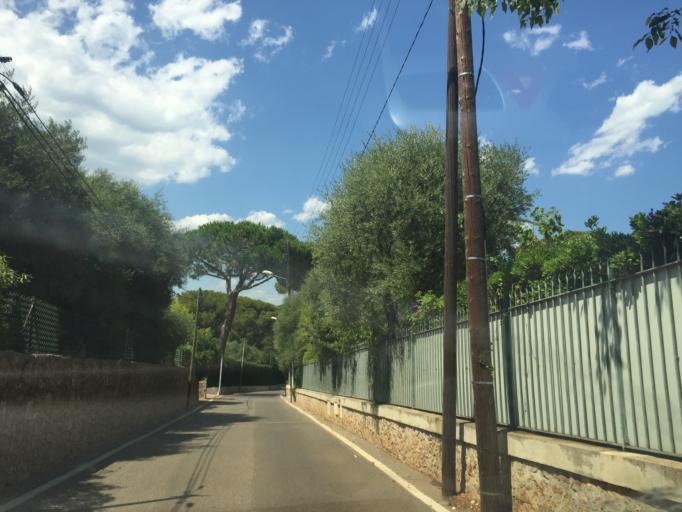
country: FR
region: Provence-Alpes-Cote d'Azur
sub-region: Departement des Alpes-Maritimes
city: Antibes
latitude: 43.5526
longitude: 7.1337
